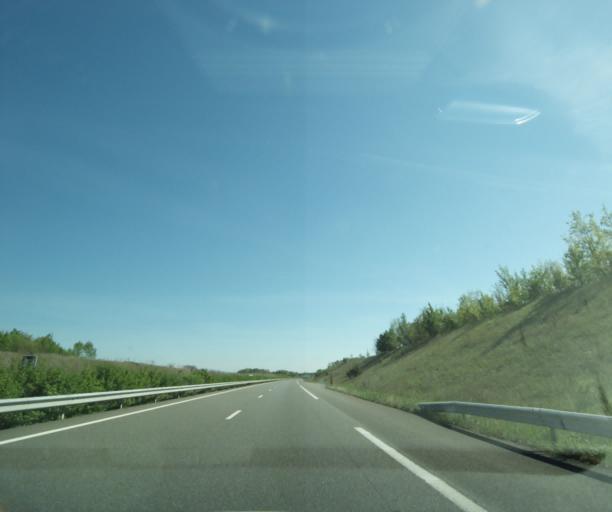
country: FR
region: Midi-Pyrenees
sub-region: Departement du Tarn-et-Garonne
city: Caussade
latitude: 44.2245
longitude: 1.5362
